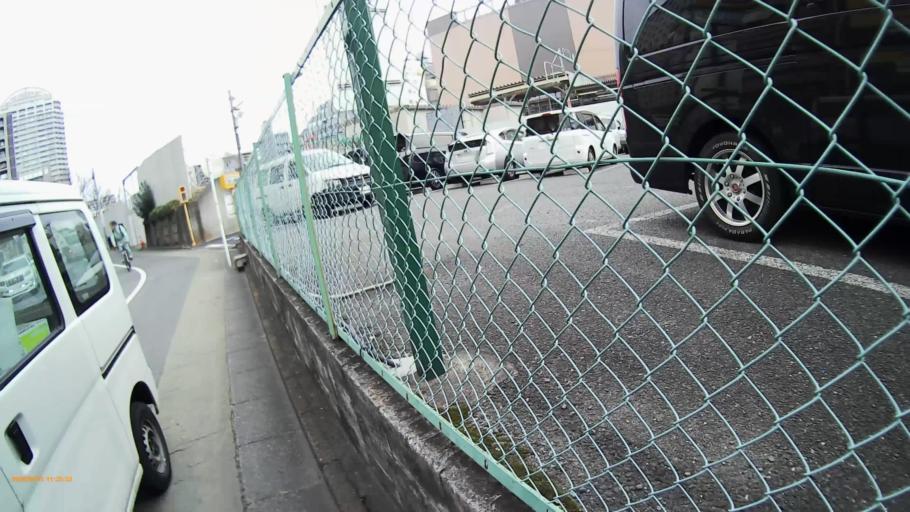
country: JP
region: Saitama
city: Kawaguchi
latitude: 35.7458
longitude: 139.7190
